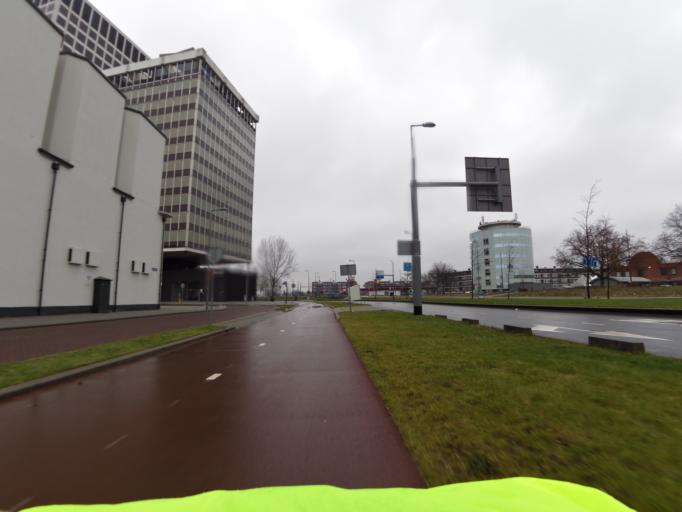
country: NL
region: South Holland
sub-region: Gemeente Rotterdam
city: Delfshaven
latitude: 51.9115
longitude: 4.4332
